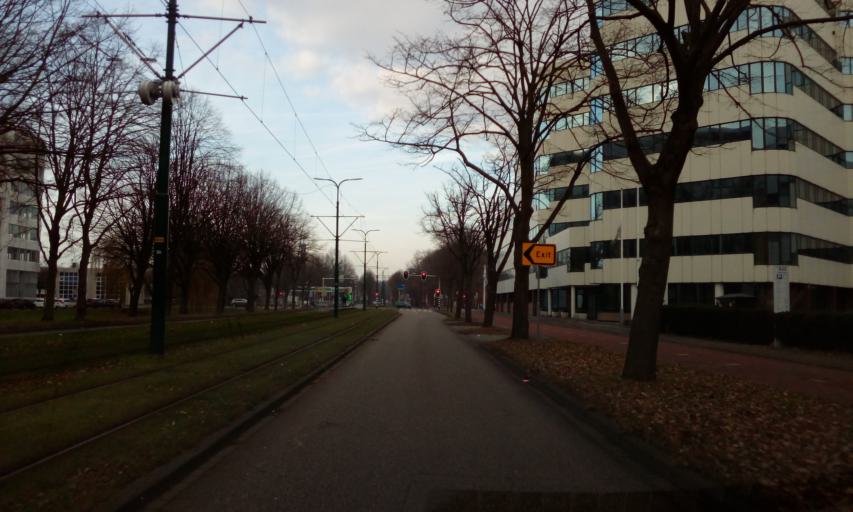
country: NL
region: South Holland
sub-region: Gemeente Rijswijk
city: Rijswijk
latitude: 52.0437
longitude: 4.3376
